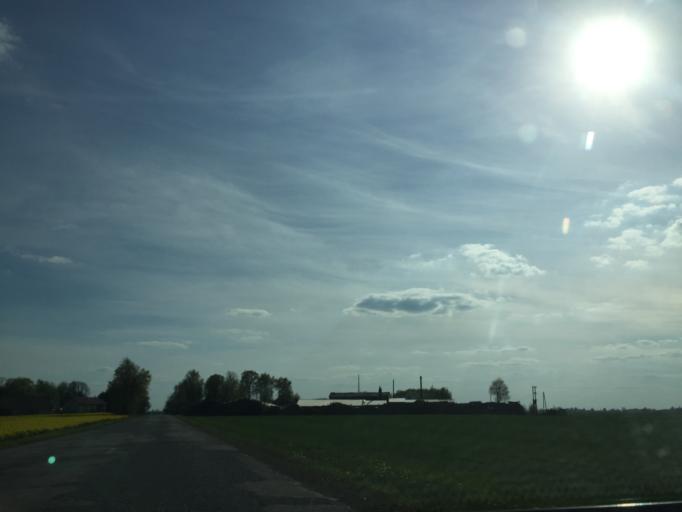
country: LV
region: Bauskas Rajons
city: Bauska
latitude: 56.4432
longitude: 24.2458
